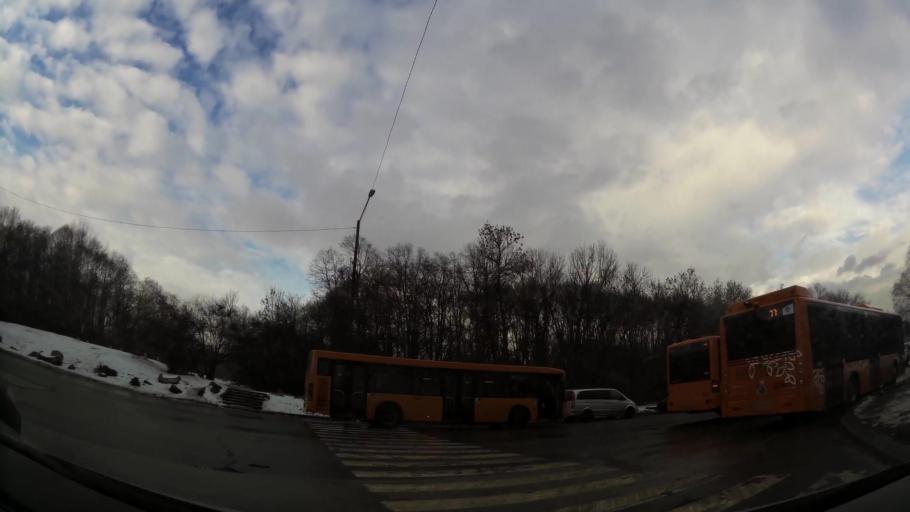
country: BG
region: Sofia-Capital
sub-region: Stolichna Obshtina
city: Sofia
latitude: 42.7014
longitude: 23.2761
